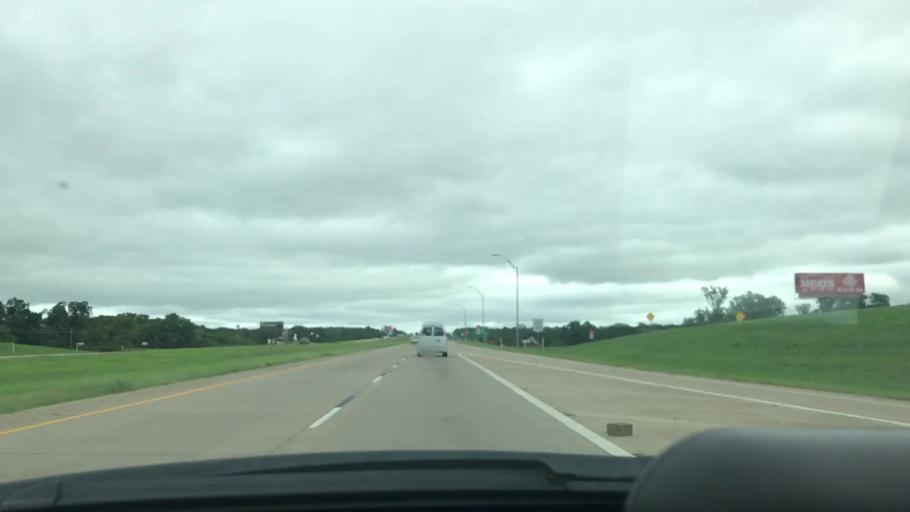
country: US
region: Texas
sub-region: Grayson County
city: Denison
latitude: 33.7230
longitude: -96.5853
